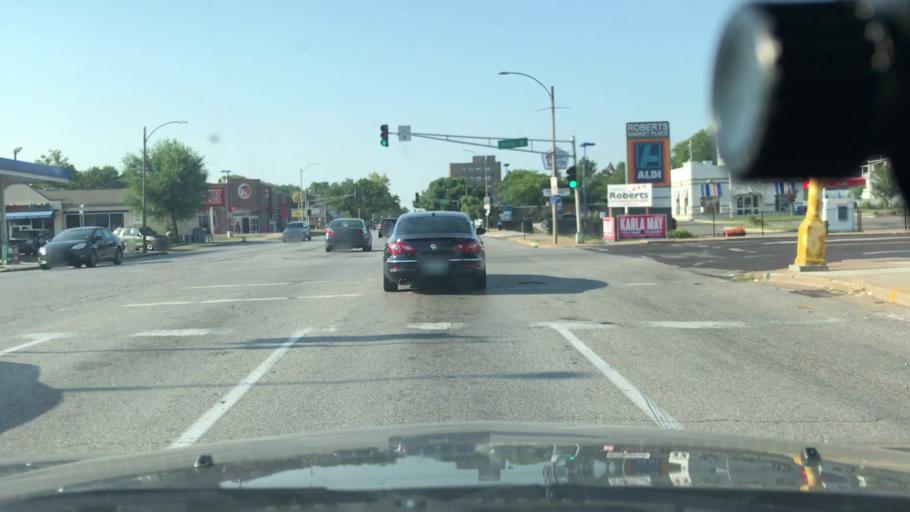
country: US
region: Missouri
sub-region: Saint Louis County
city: Hillsdale
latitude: 38.6514
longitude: -90.2635
